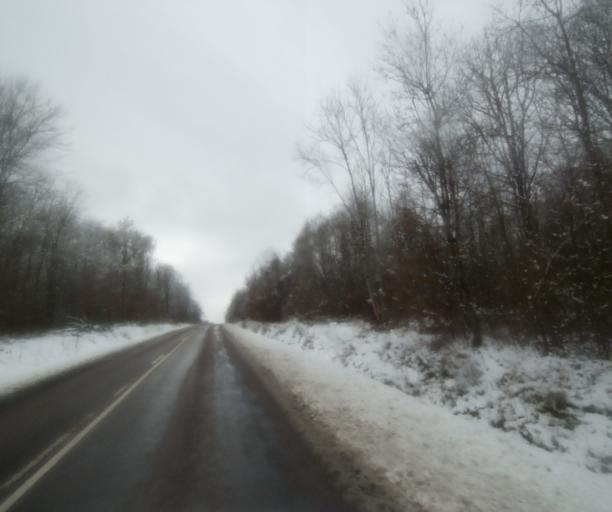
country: FR
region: Champagne-Ardenne
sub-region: Departement de la Haute-Marne
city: Wassy
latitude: 48.4952
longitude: 4.9204
